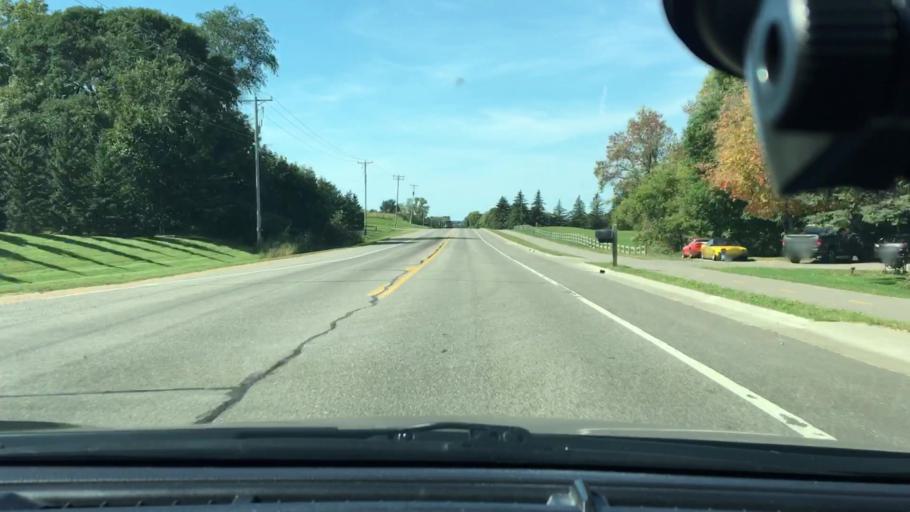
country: US
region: Minnesota
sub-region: Wright County
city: Hanover
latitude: 45.1525
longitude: -93.6460
